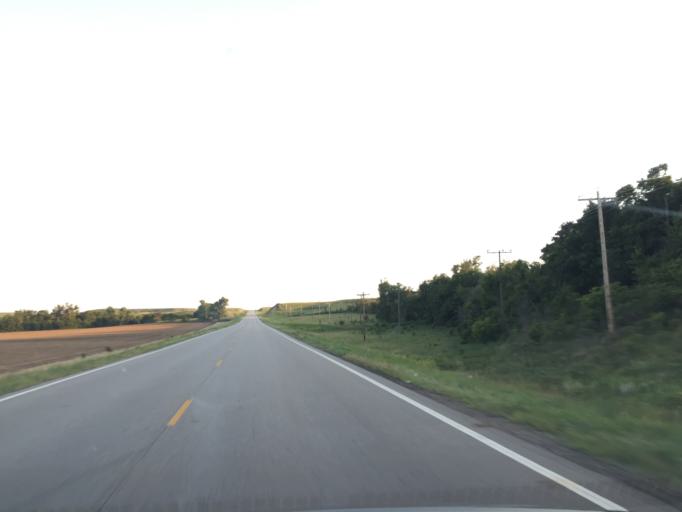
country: US
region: Kansas
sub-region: Ellsworth County
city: Ellsworth
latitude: 38.6219
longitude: -98.2019
